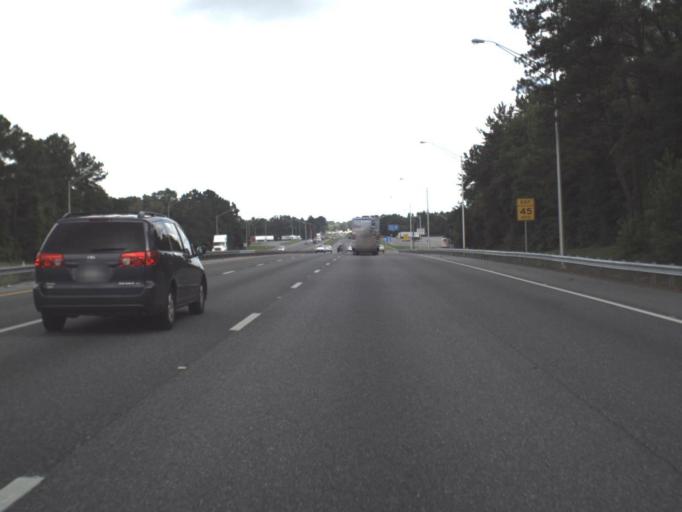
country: US
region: Florida
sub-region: Alachua County
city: High Springs
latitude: 29.9728
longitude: -82.5762
